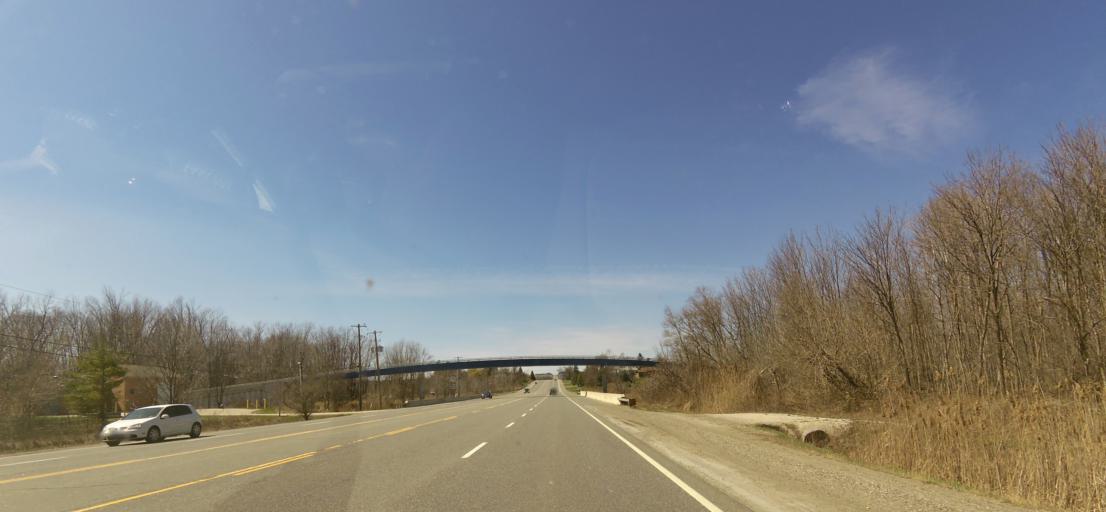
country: CA
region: Ontario
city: Orangeville
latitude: 43.8115
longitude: -79.9298
